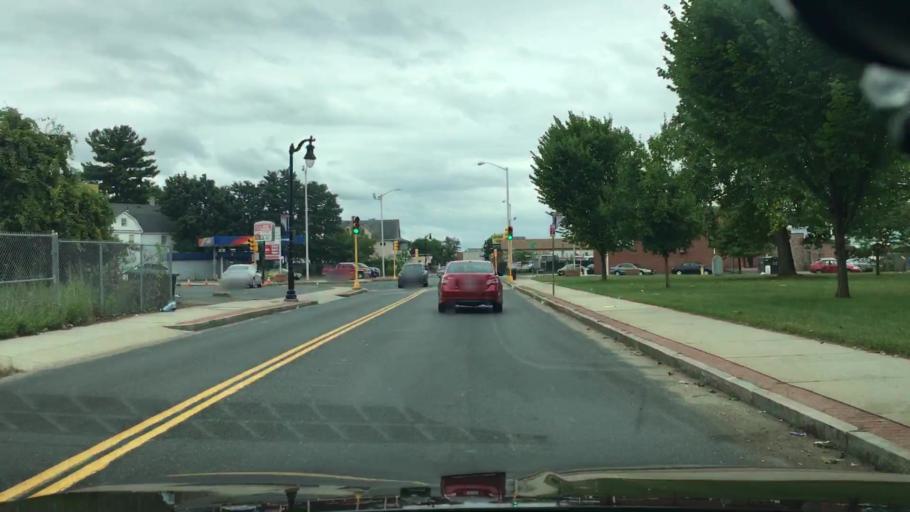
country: US
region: Massachusetts
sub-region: Hampden County
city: Springfield
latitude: 42.1018
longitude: -72.5681
